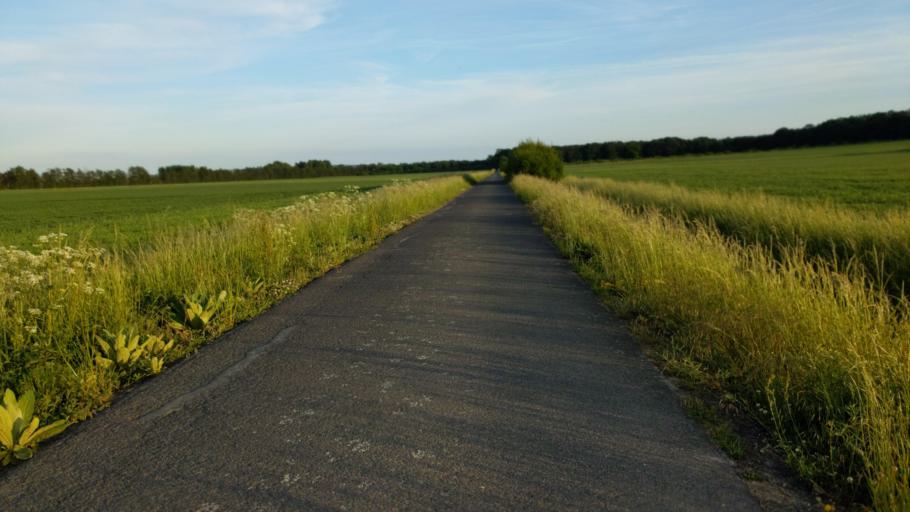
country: DE
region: Lower Saxony
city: Sickte
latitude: 52.2314
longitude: 10.5915
